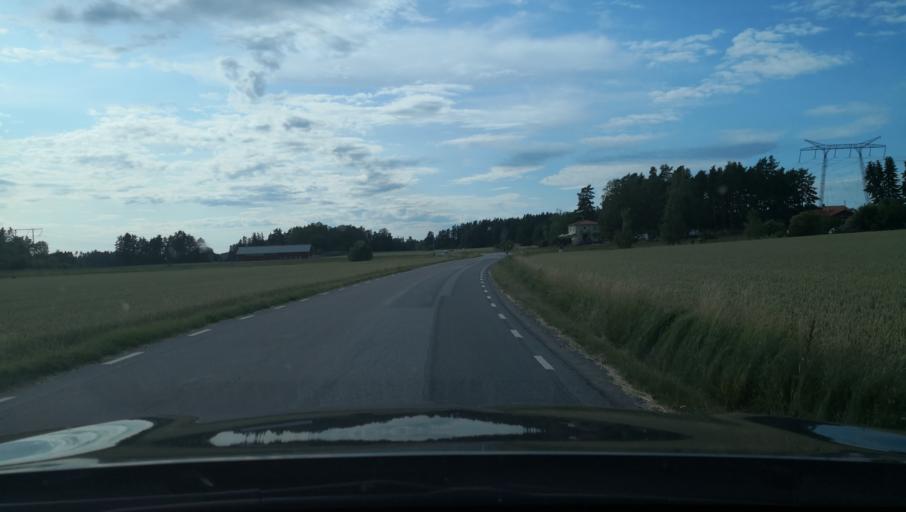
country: SE
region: Uppsala
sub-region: Enkopings Kommun
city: Orsundsbro
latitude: 59.6806
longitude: 17.4079
